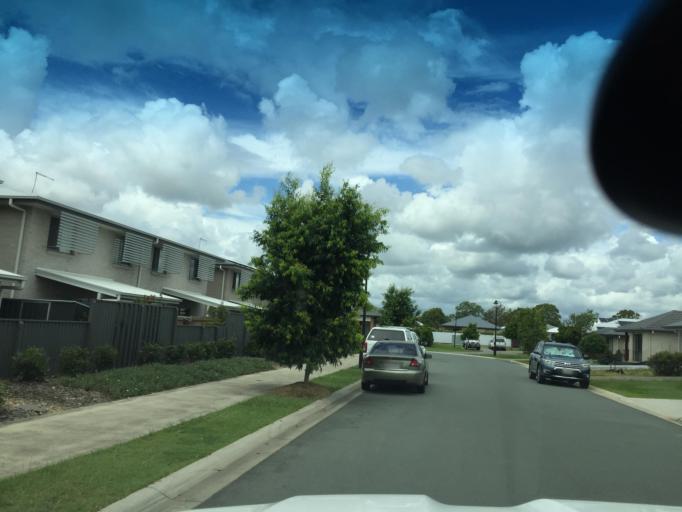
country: AU
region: Queensland
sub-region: Moreton Bay
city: Caboolture South
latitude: -27.0952
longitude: 152.9571
